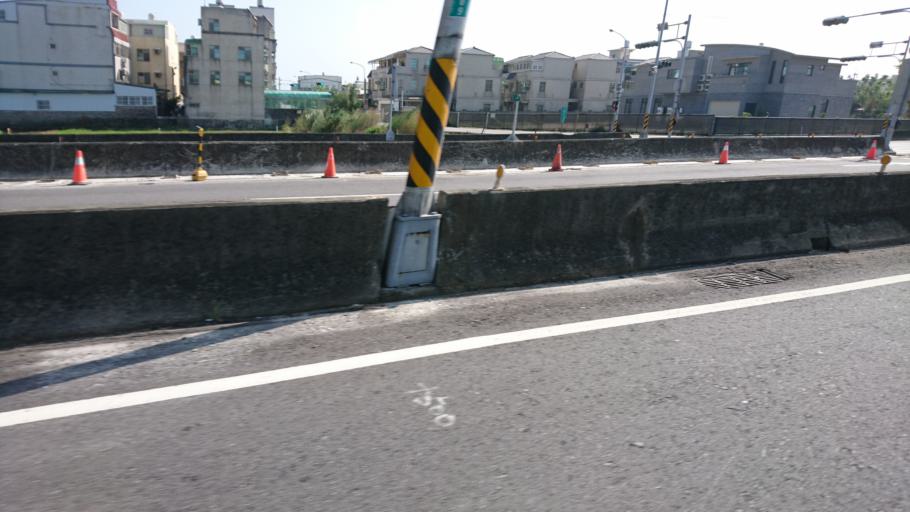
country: TW
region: Taiwan
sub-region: Miaoli
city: Miaoli
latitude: 24.6915
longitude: 120.8566
